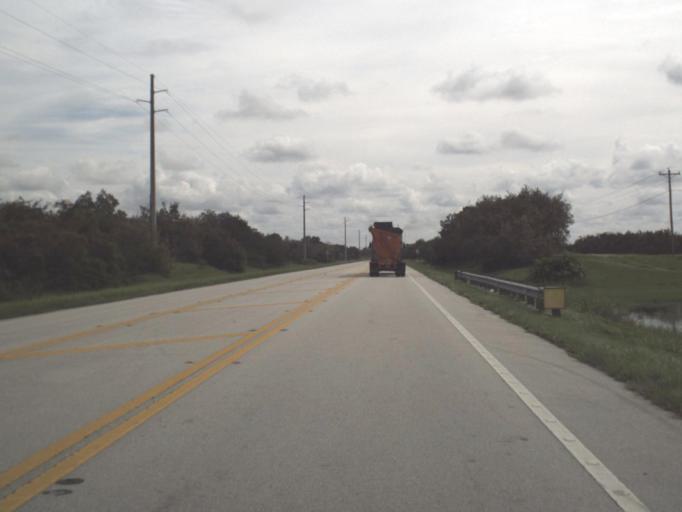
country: US
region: Florida
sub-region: Highlands County
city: Lake Placid
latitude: 27.2082
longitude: -81.3120
